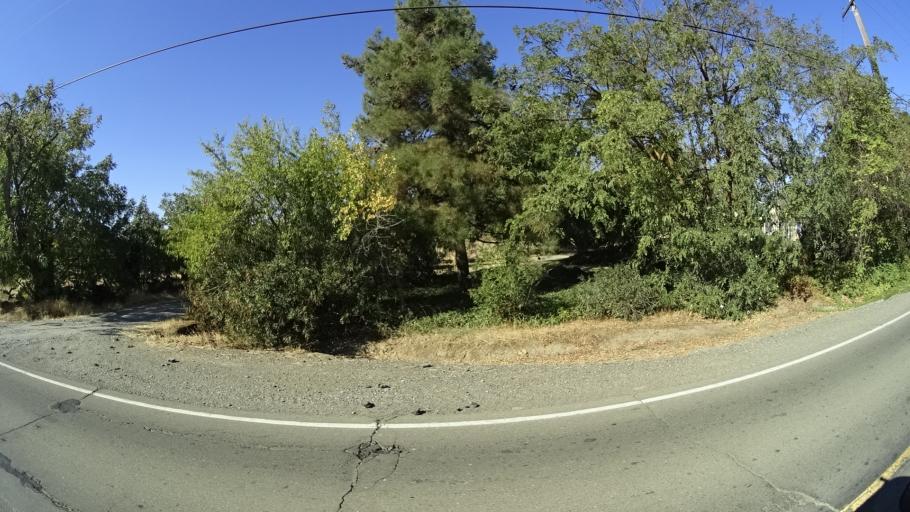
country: US
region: California
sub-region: Yolo County
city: Cottonwood
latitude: 38.5949
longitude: -121.9714
